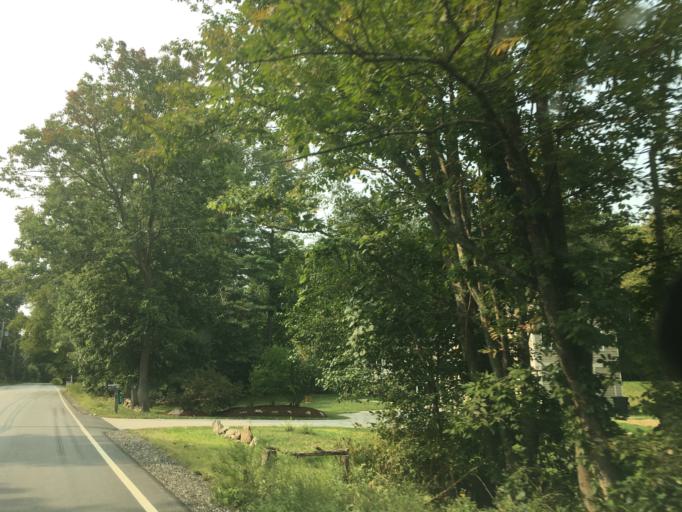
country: US
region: New Hampshire
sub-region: Rockingham County
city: Stratham Station
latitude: 43.0168
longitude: -70.8895
